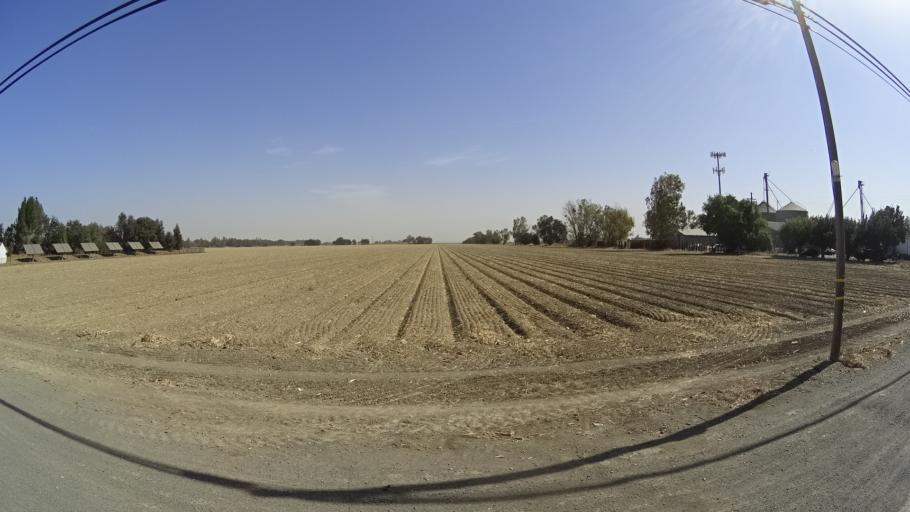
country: US
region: California
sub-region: Yolo County
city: Davis
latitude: 38.5346
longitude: -121.6946
